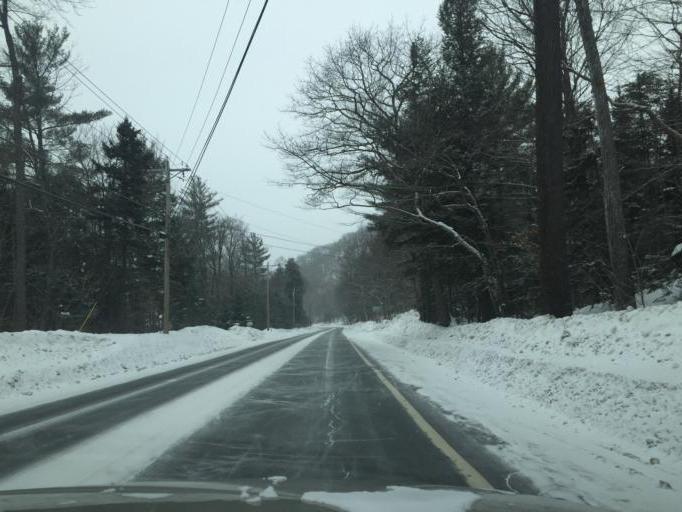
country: US
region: New Hampshire
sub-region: Carroll County
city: North Conway
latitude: 44.1934
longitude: -71.2304
